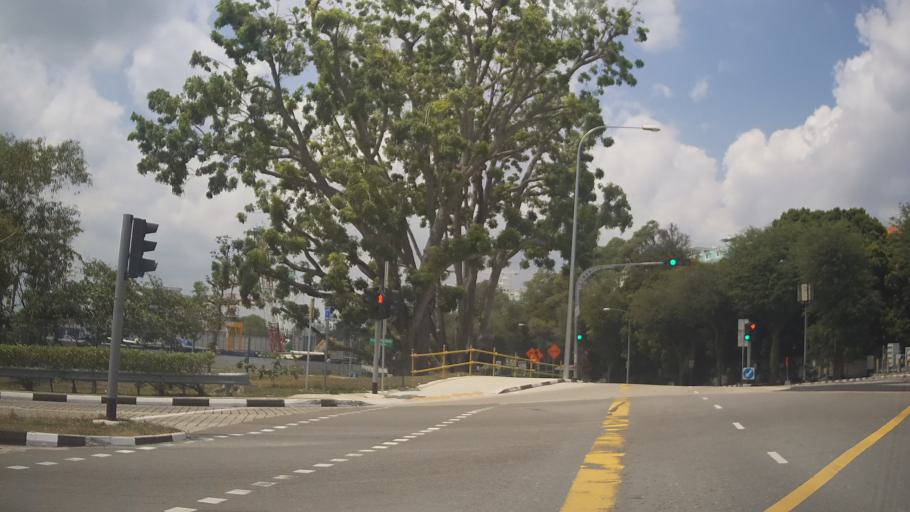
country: SG
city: Singapore
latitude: 1.3183
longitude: 103.9523
